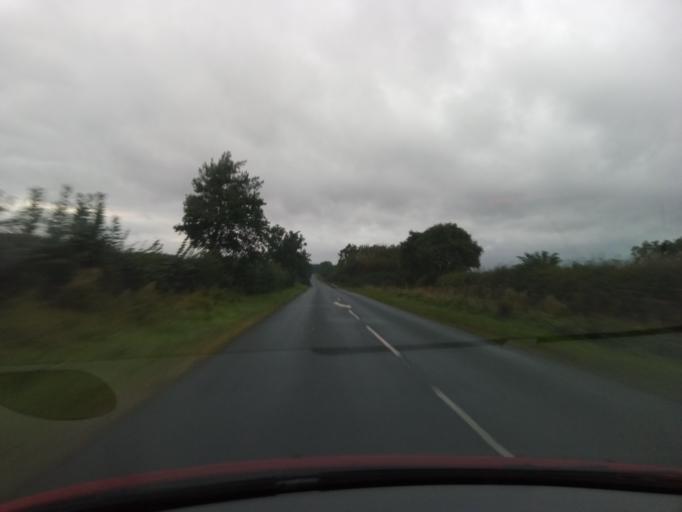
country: GB
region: England
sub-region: Darlington
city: High Coniscliffe
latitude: 54.5092
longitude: -1.6713
